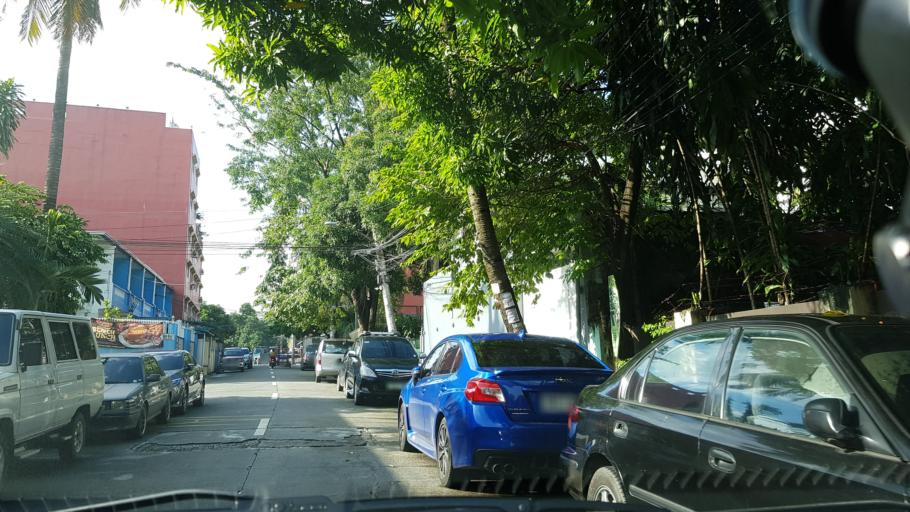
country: PH
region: Metro Manila
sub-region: Quezon City
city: Quezon City
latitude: 14.6428
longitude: 121.0528
